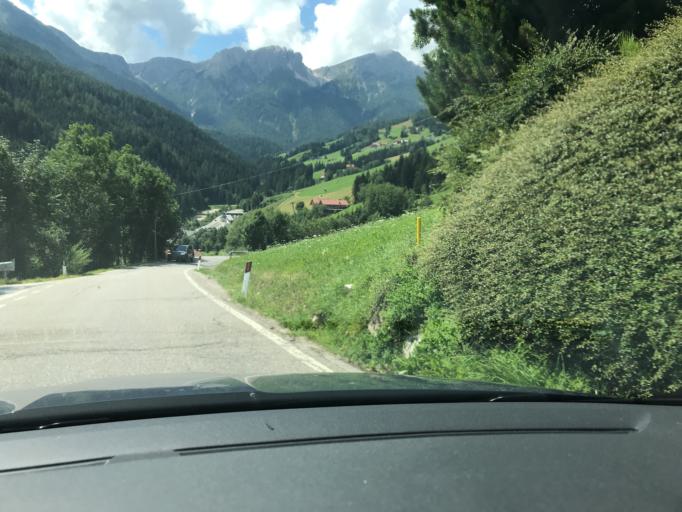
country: IT
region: Trentino-Alto Adige
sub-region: Bolzano
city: Valdaora di Mezzo
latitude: 46.7517
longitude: 12.0122
